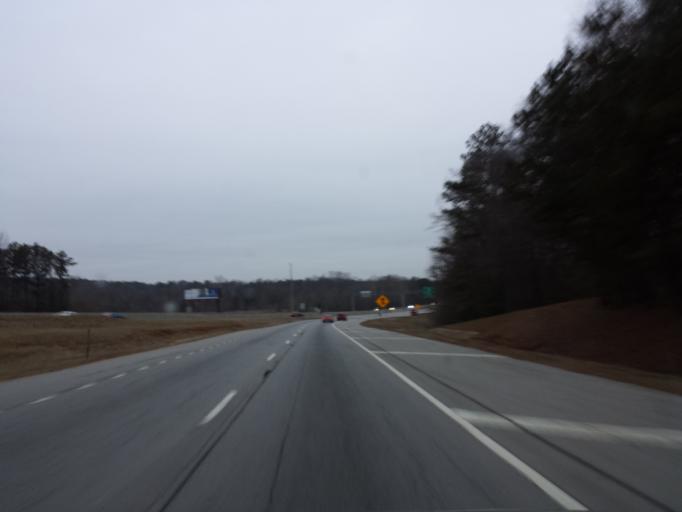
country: US
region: Georgia
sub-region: Fulton County
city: Alpharetta
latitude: 34.0373
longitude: -84.3140
